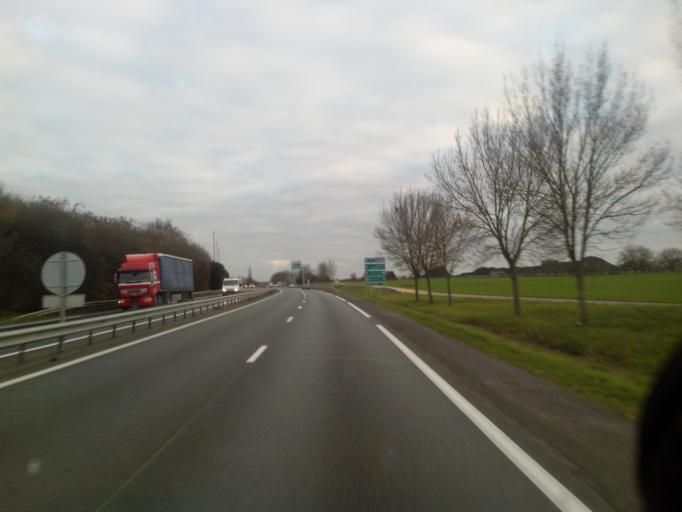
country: FR
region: Poitou-Charentes
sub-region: Departement de la Vienne
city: Migne-Auxances
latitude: 46.6199
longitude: 0.3055
